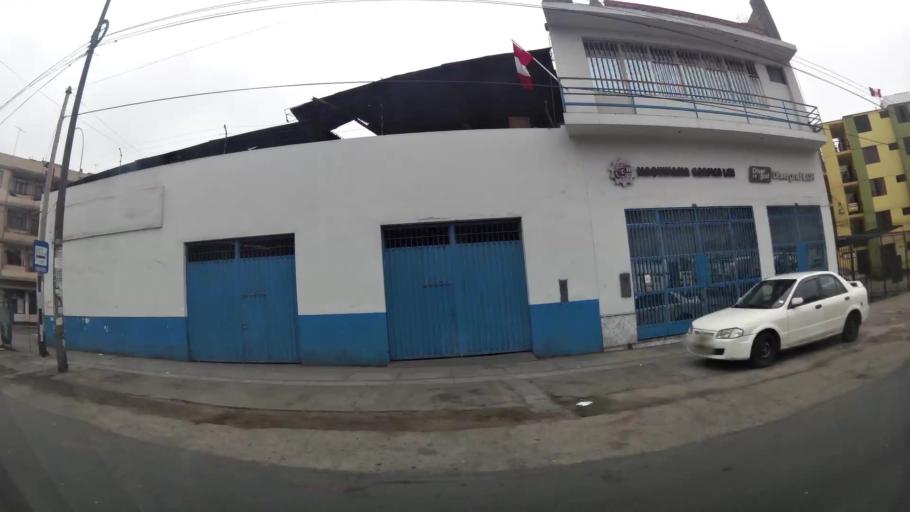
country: PE
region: Lima
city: Lima
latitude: -12.0652
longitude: -77.0445
